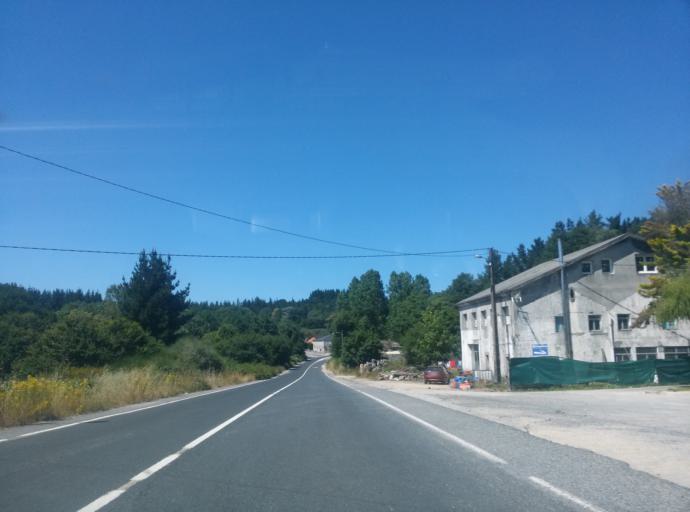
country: ES
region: Galicia
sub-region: Provincia de Lugo
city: Mos
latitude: 43.0957
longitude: -7.4780
